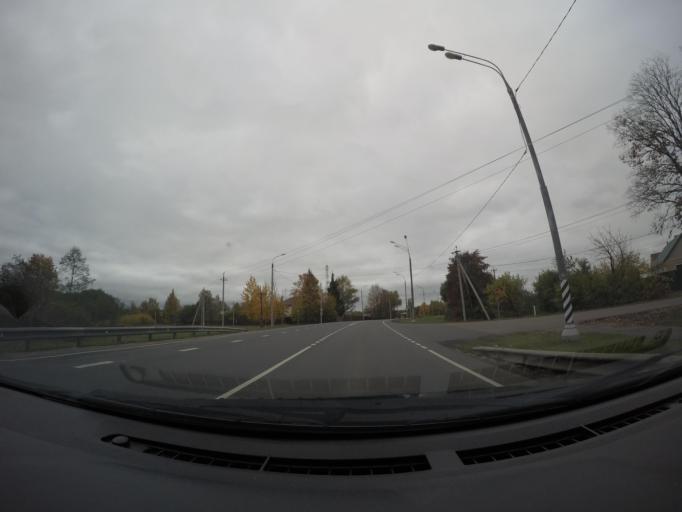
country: RU
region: Moskovskaya
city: Ruza
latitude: 55.7353
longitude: 36.2225
